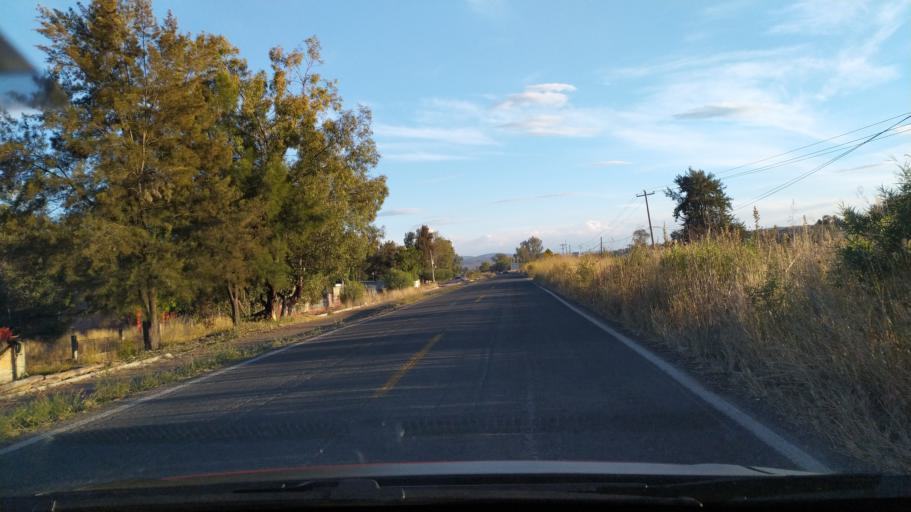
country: MX
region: Guanajuato
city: Ciudad Manuel Doblado
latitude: 20.7496
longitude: -101.9616
